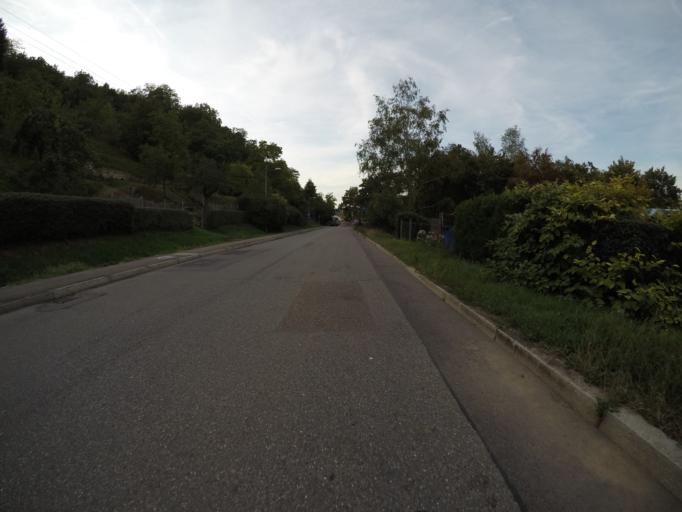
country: DE
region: Baden-Wuerttemberg
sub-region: Regierungsbezirk Stuttgart
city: Ostfildern
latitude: 48.7530
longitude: 9.2613
